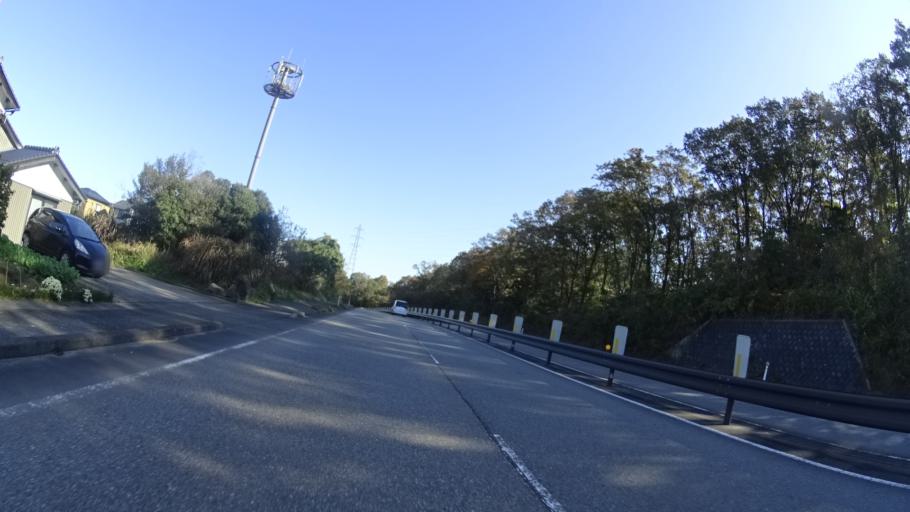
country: JP
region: Ishikawa
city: Komatsu
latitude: 36.3932
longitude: 136.5018
